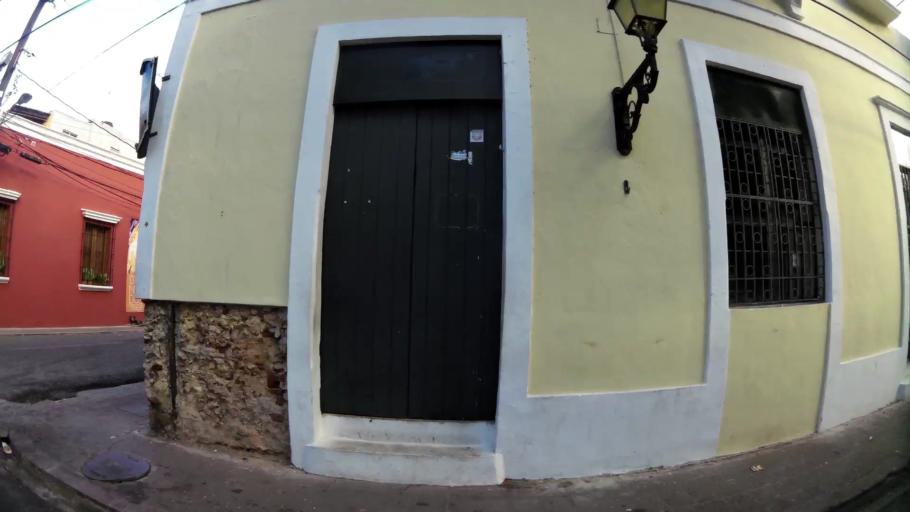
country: DO
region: Nacional
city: Ciudad Nueva
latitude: 18.4709
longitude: -69.8871
